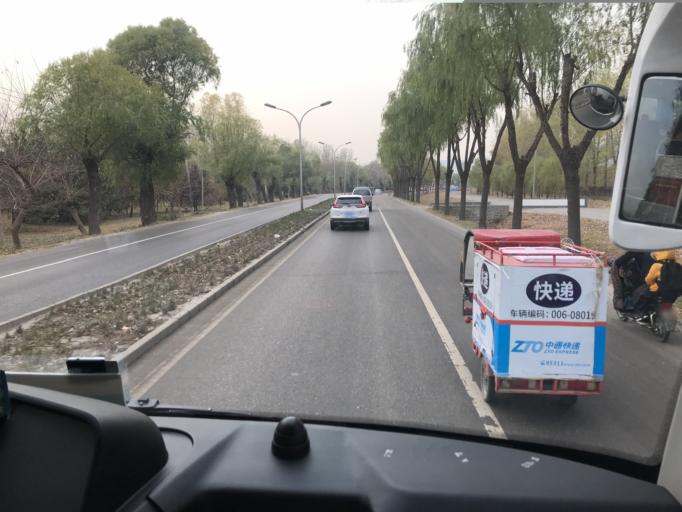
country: CN
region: Beijing
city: Wenquan
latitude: 40.0826
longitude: 116.2106
